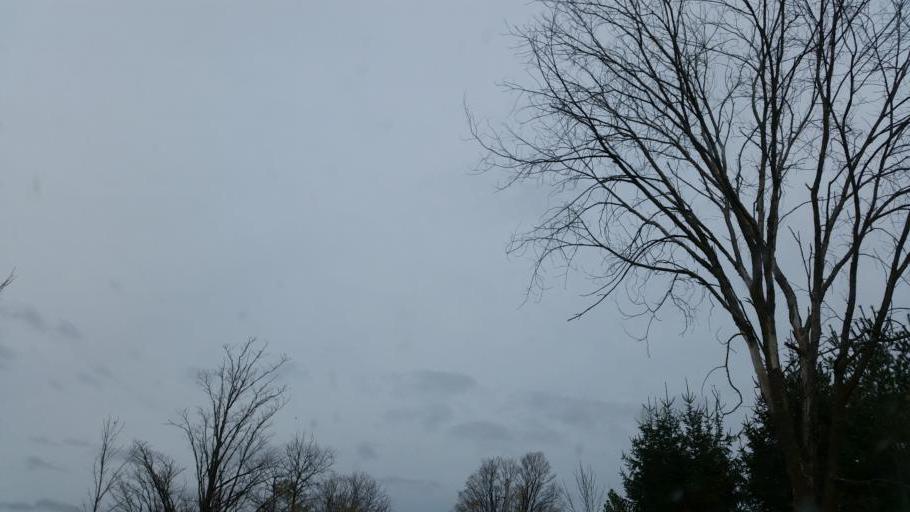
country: CA
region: Ontario
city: Wingham
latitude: 43.9898
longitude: -81.3360
